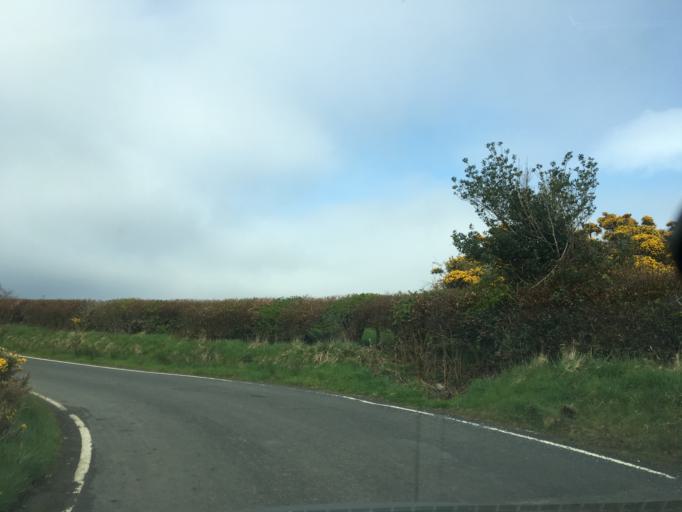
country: GB
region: Scotland
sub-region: Argyll and Bute
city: Rothesay
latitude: 55.8351
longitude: -5.0395
